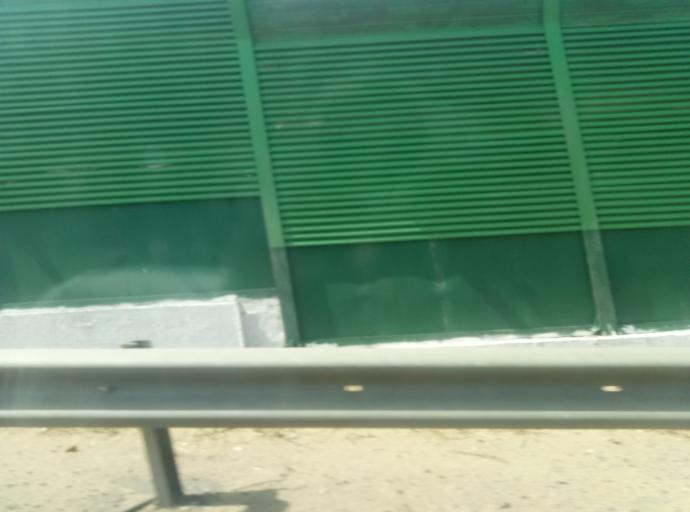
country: RU
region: Tula
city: Dubovka
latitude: 53.8669
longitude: 38.0678
